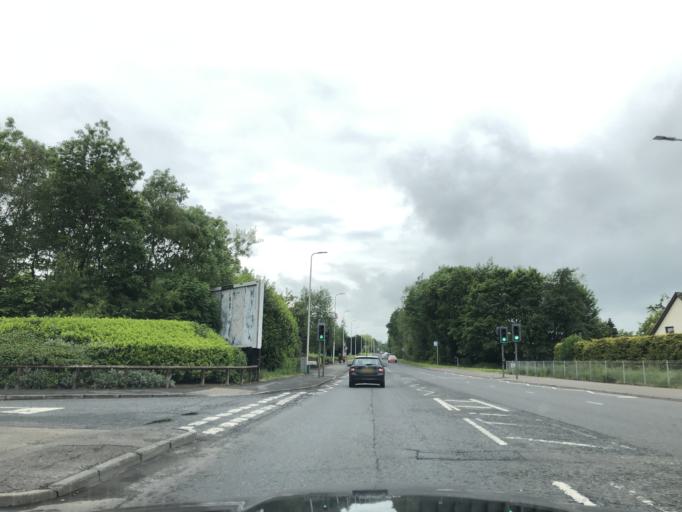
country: GB
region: Northern Ireland
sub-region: Lisburn District
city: Lisburn
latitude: 54.5157
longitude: -6.0568
